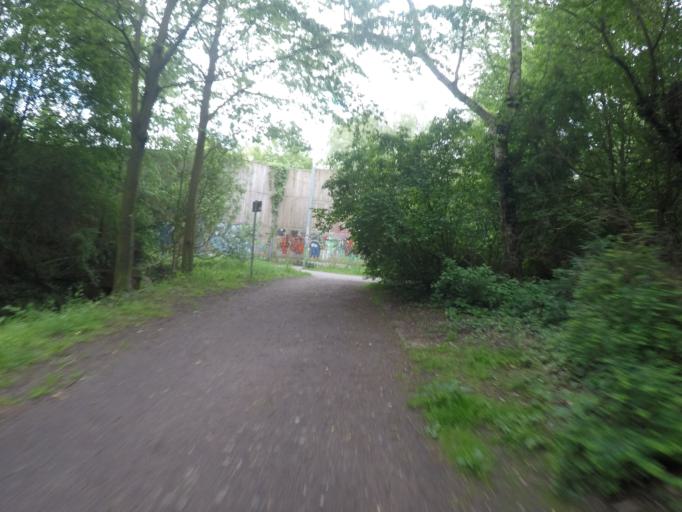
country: DE
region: Schleswig-Holstein
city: Bonningstedt
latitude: 53.6468
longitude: 9.9258
